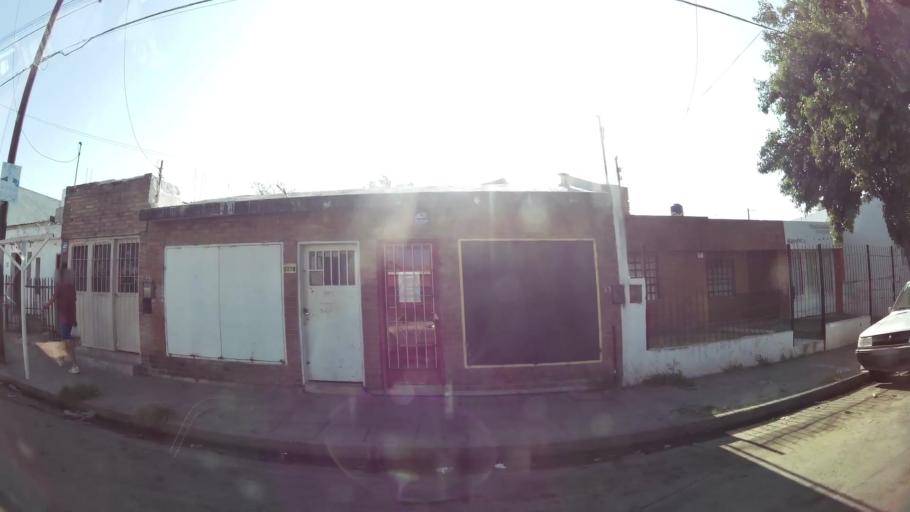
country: AR
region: Cordoba
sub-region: Departamento de Capital
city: Cordoba
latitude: -31.4731
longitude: -64.2249
